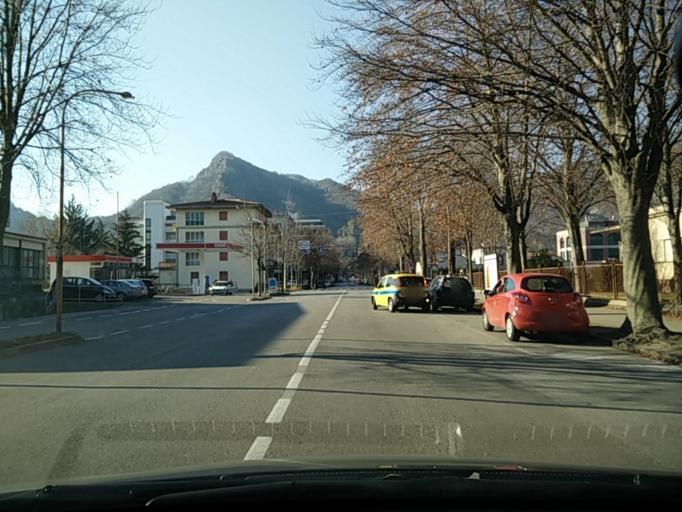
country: IT
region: Veneto
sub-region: Provincia di Treviso
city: Vittorio Veneto
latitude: 45.9908
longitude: 12.3016
